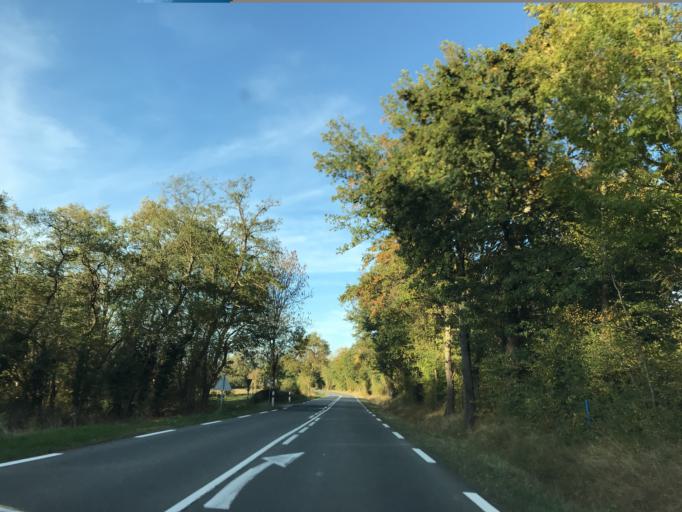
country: FR
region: Auvergne
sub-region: Departement du Puy-de-Dome
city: Puy-Guillaume
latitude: 45.9746
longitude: 3.4808
